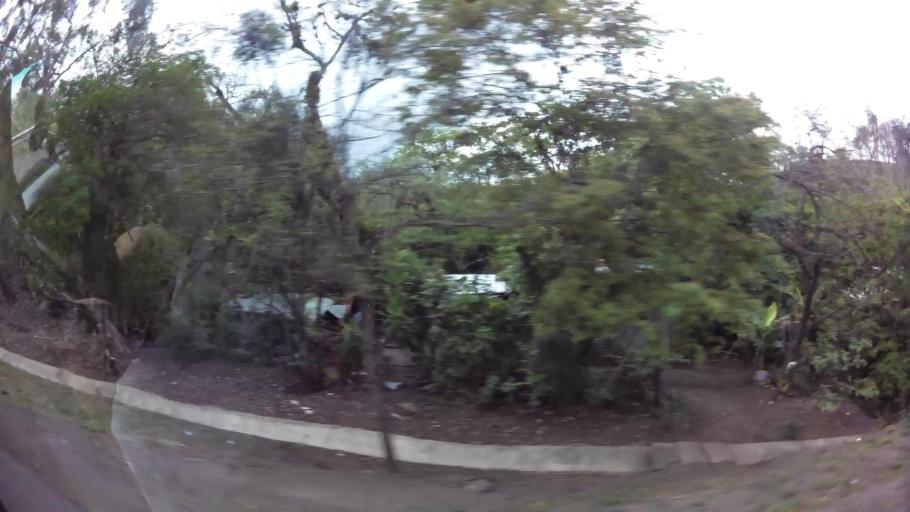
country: NI
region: Matagalpa
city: Matagalpa
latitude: 12.9141
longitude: -85.9436
